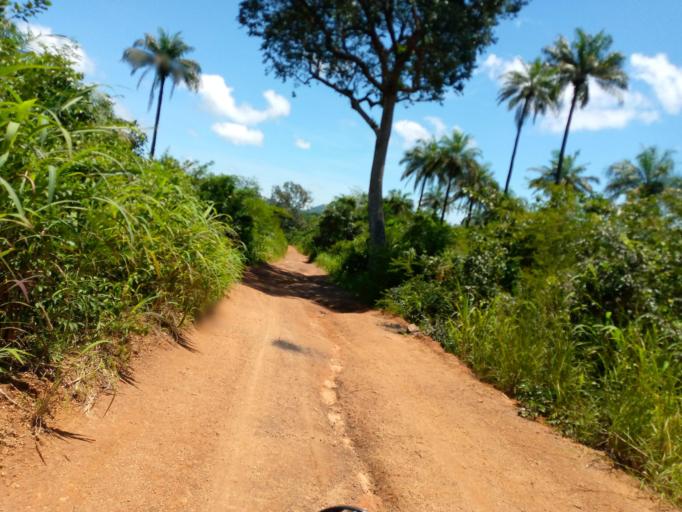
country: SL
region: Northern Province
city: Binkolo
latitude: 9.1169
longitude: -12.1745
